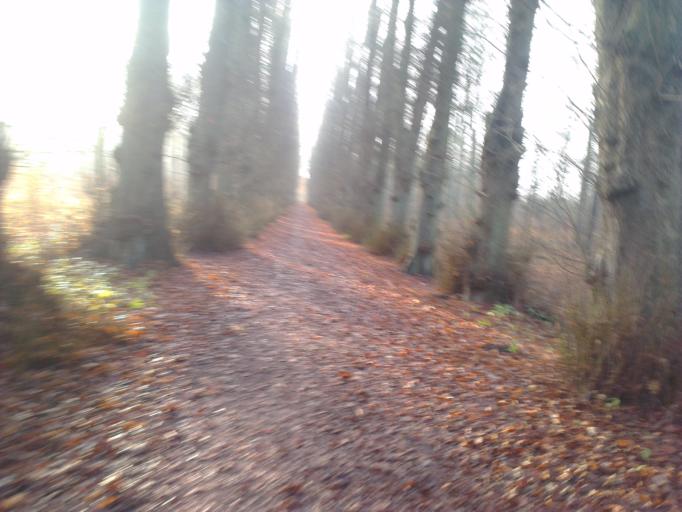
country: DK
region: Capital Region
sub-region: Frederikssund Kommune
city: Jaegerspris
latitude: 55.8618
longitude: 11.9853
